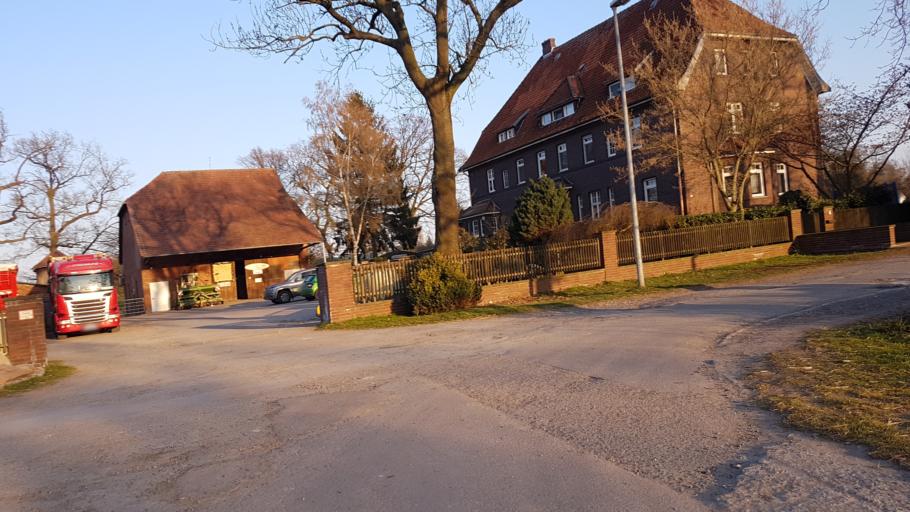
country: DE
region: Lower Saxony
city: Langenhagen
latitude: 52.4259
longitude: 9.7005
